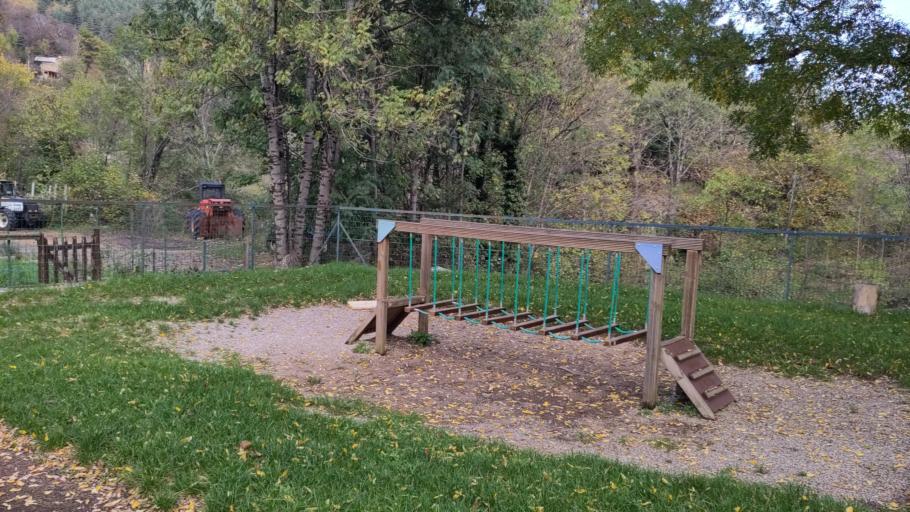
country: FR
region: Rhone-Alpes
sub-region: Departement de l'Ardeche
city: Le Cheylard
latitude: 44.8222
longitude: 4.4298
